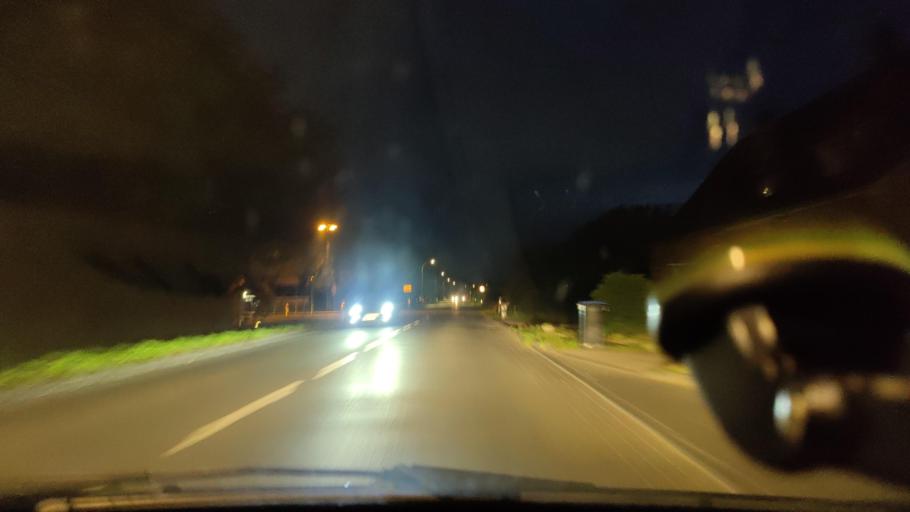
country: DE
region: North Rhine-Westphalia
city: Rheinberg
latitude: 51.5689
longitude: 6.5795
